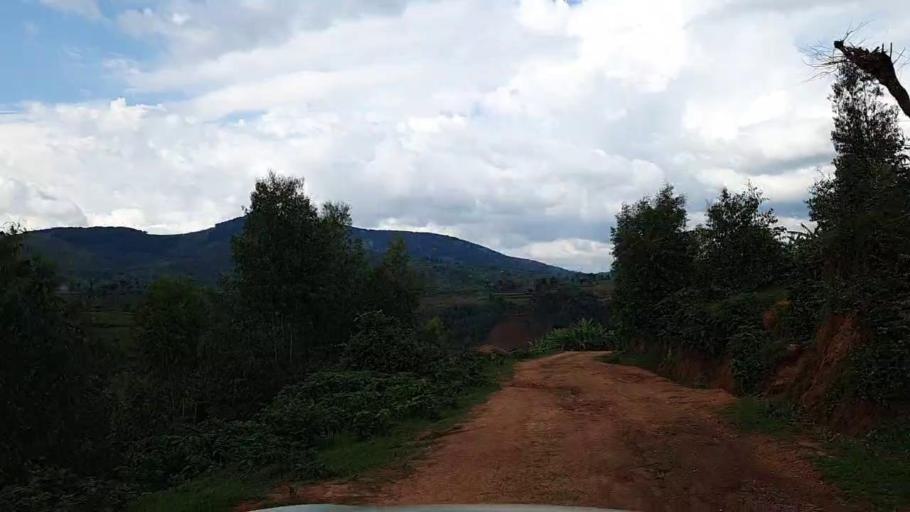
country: RW
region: Southern Province
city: Gikongoro
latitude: -2.4186
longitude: 29.6542
